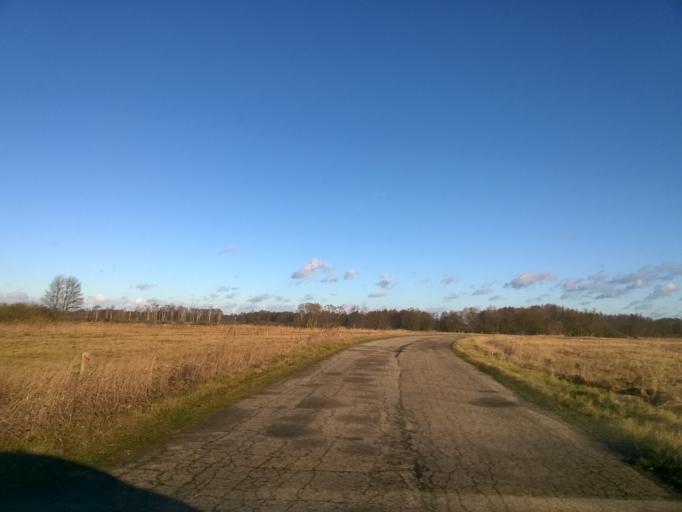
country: PL
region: Kujawsko-Pomorskie
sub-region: Powiat nakielski
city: Sadki
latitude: 53.0966
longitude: 17.4297
